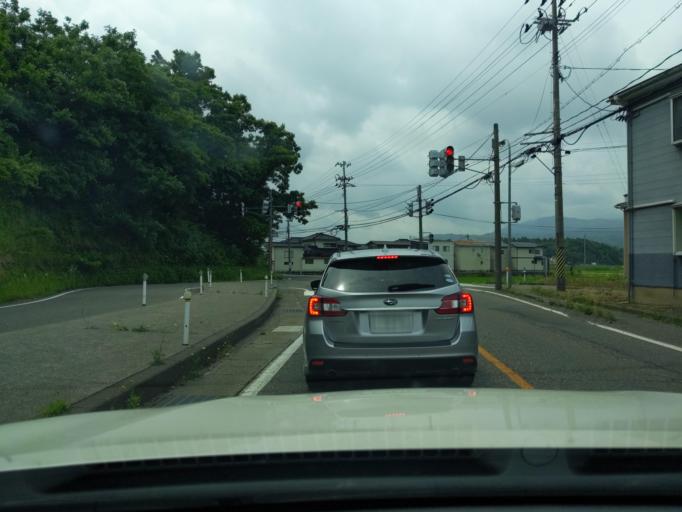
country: JP
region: Niigata
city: Kashiwazaki
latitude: 37.3534
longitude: 138.5694
